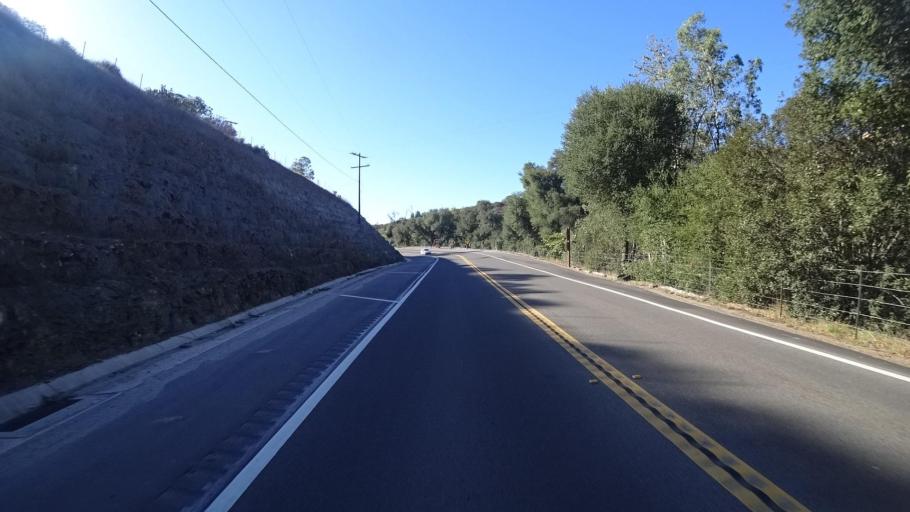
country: MX
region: Baja California
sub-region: Tijuana
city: Villa del Campo
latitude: 32.6350
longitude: -116.7651
